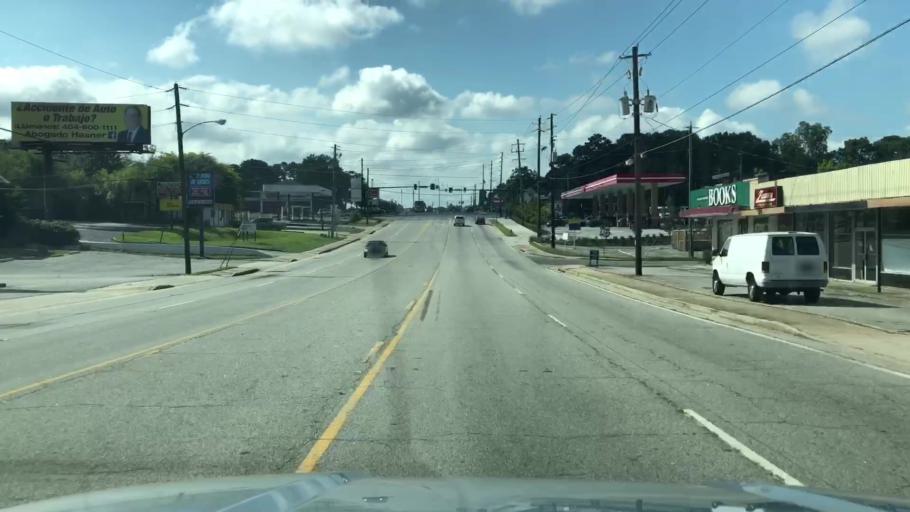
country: US
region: Georgia
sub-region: DeKalb County
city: Chamblee
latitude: 33.8671
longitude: -84.3095
